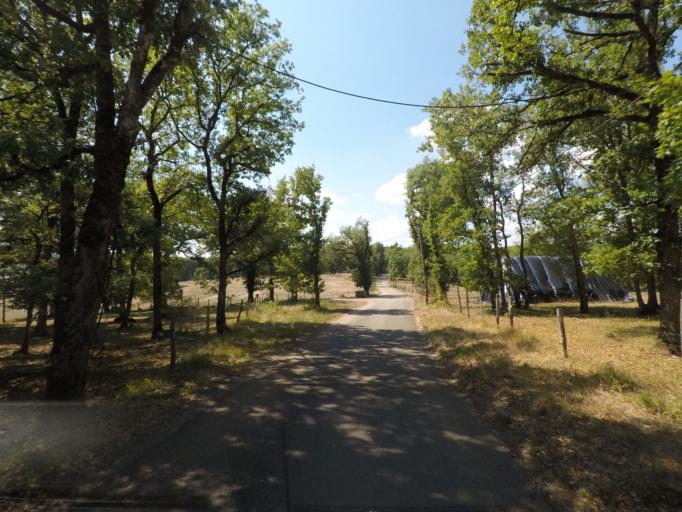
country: FR
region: Midi-Pyrenees
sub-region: Departement du Lot
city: Cahors
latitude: 44.5334
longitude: 1.6093
